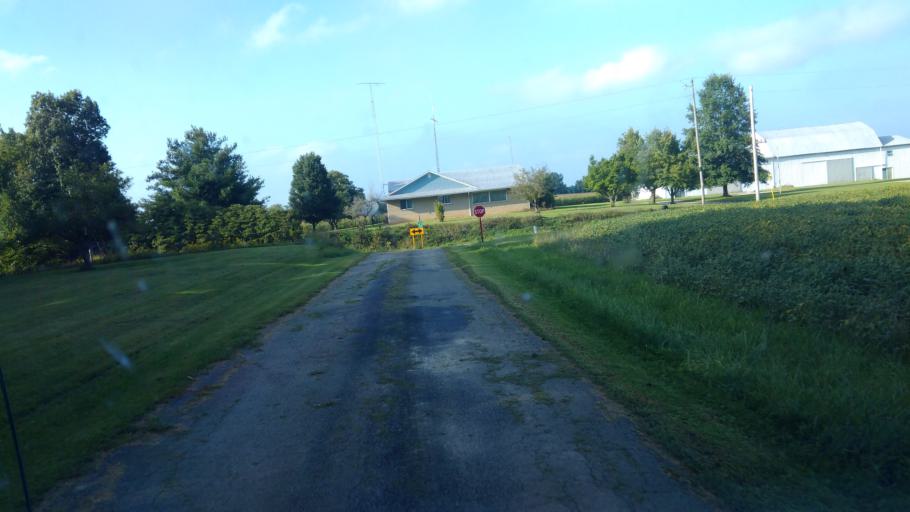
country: US
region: Ohio
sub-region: Wyandot County
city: Upper Sandusky
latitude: 40.7732
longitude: -83.3602
